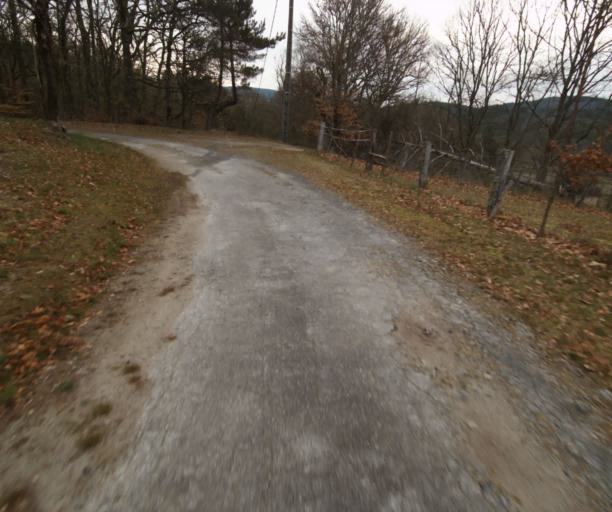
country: FR
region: Limousin
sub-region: Departement de la Correze
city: Correze
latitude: 45.4286
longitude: 1.8516
